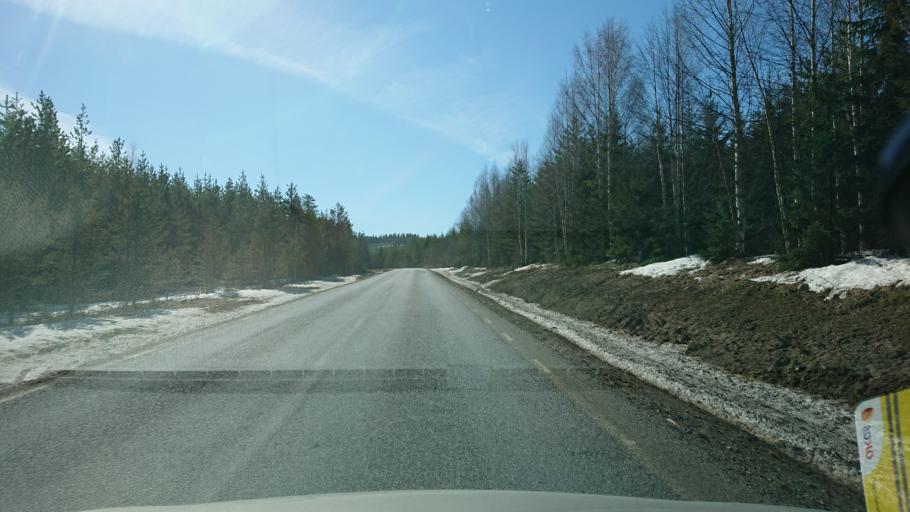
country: SE
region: Vaesterbotten
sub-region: Dorotea Kommun
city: Dorotea
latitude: 64.0011
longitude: 16.3048
